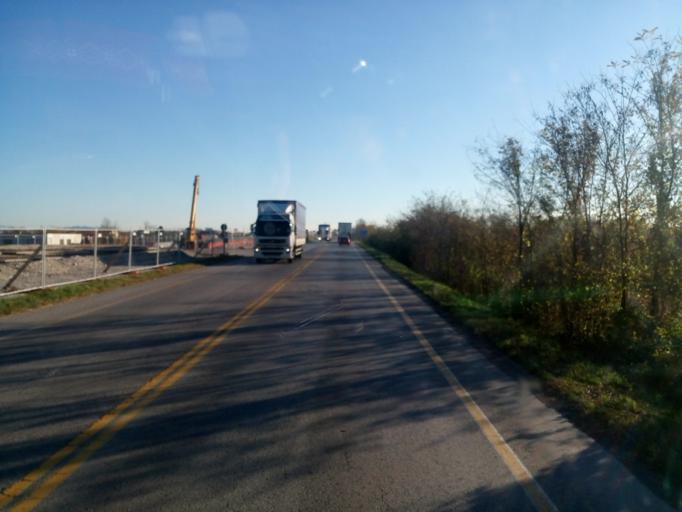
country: IT
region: Veneto
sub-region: Provincia di Vicenza
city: Nove
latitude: 45.7385
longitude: 11.6860
